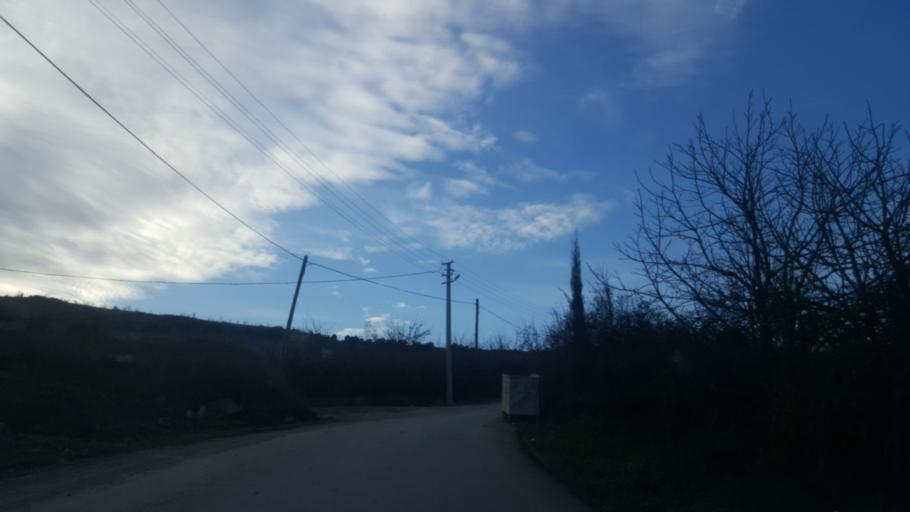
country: TR
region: Kocaeli
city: Tavsanli
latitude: 40.8444
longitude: 29.5556
